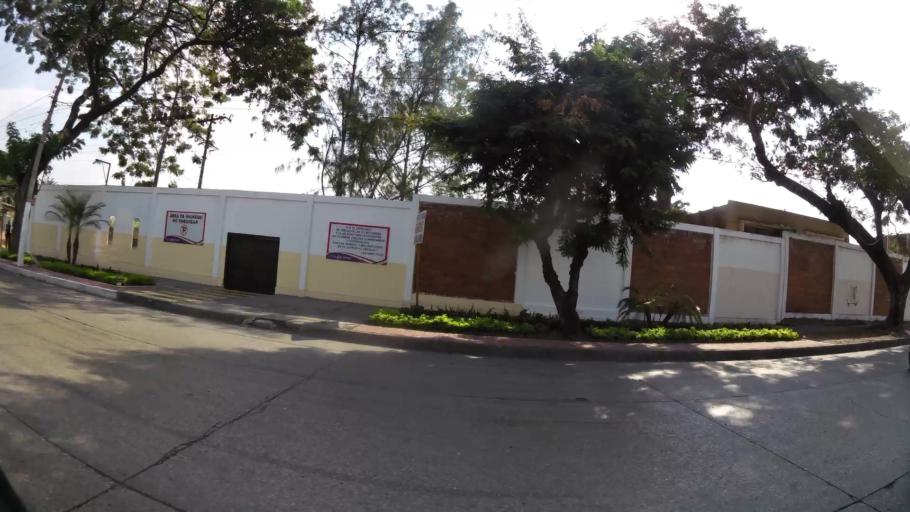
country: EC
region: Guayas
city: Guayaquil
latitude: -2.1385
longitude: -79.9283
